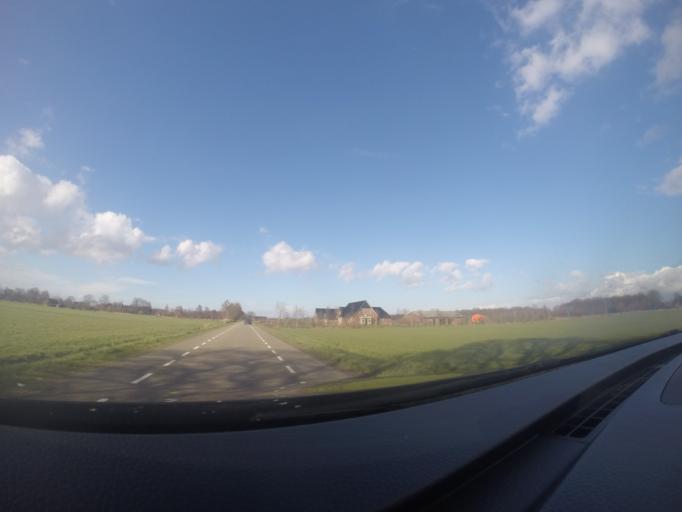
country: NL
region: Gelderland
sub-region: Oude IJsselstreek
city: Varsseveld
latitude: 52.0329
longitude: 6.4526
